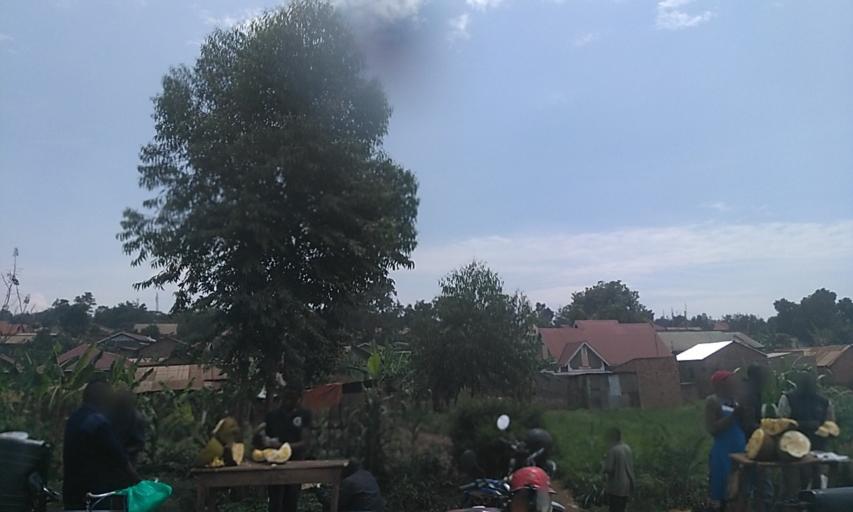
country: UG
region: Central Region
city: Kampala Central Division
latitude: 0.3466
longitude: 32.5493
